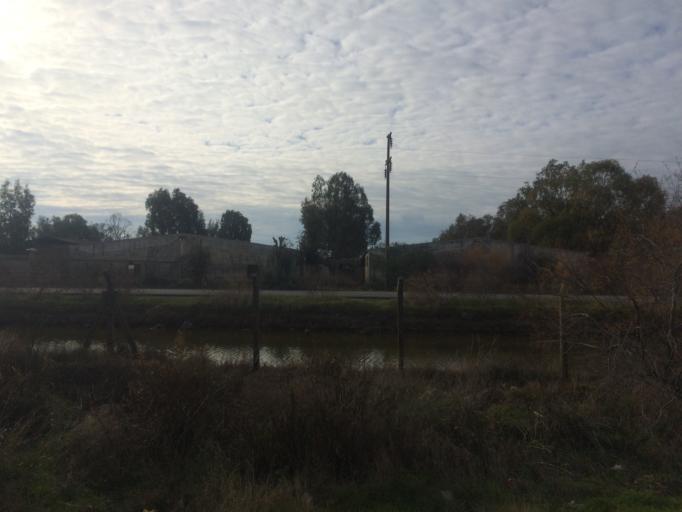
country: TR
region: Izmir
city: Karsiyaka
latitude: 38.4917
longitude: 26.9443
